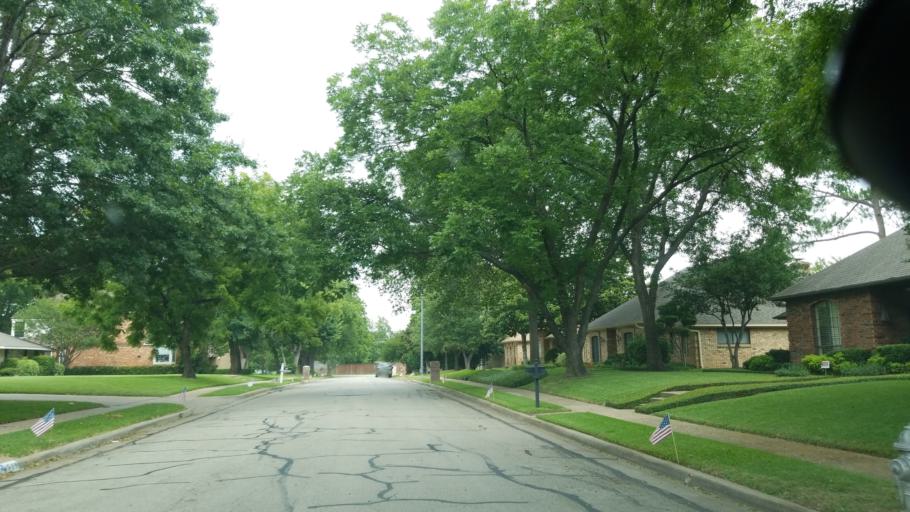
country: US
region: Texas
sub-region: Dallas County
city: Irving
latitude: 32.8509
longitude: -96.9521
